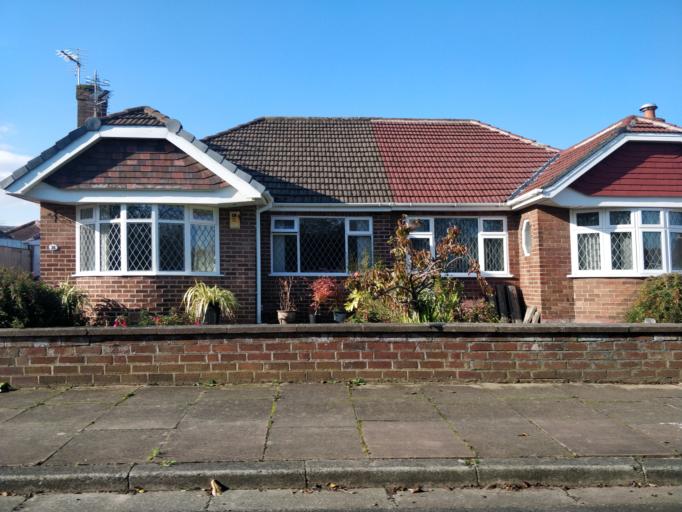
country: GB
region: England
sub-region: Lancashire
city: Banks
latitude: 53.6723
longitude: -2.9538
